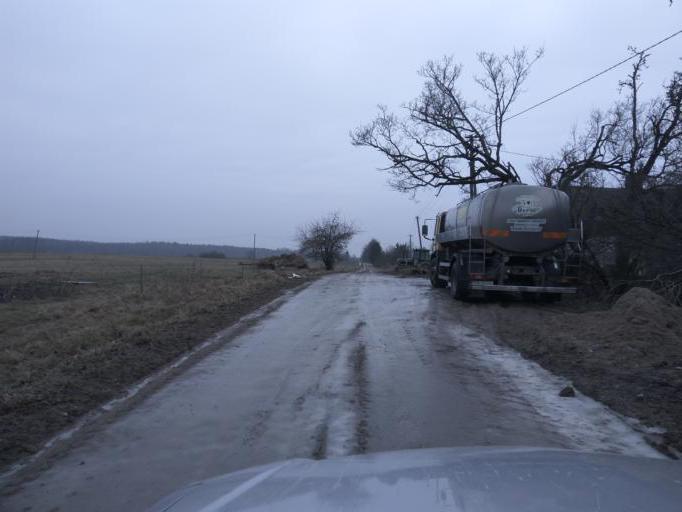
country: LV
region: Durbe
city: Liegi
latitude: 56.6720
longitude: 21.3553
